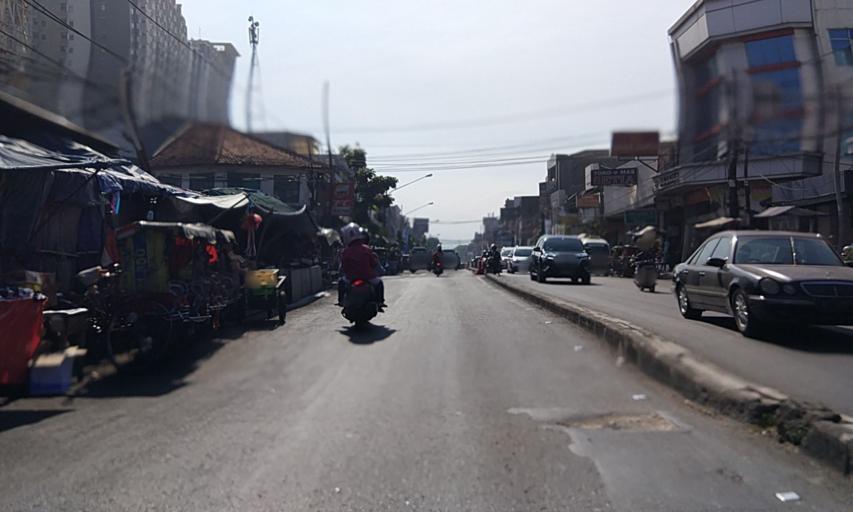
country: ID
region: West Java
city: Bandung
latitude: -6.9085
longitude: 107.6435
